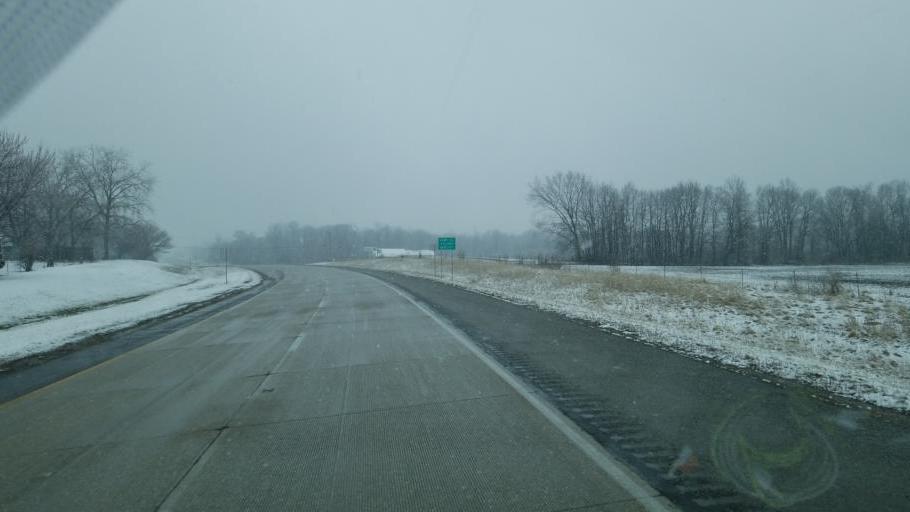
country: US
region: Indiana
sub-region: Grant County
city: Marion
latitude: 40.5522
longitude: -85.6369
